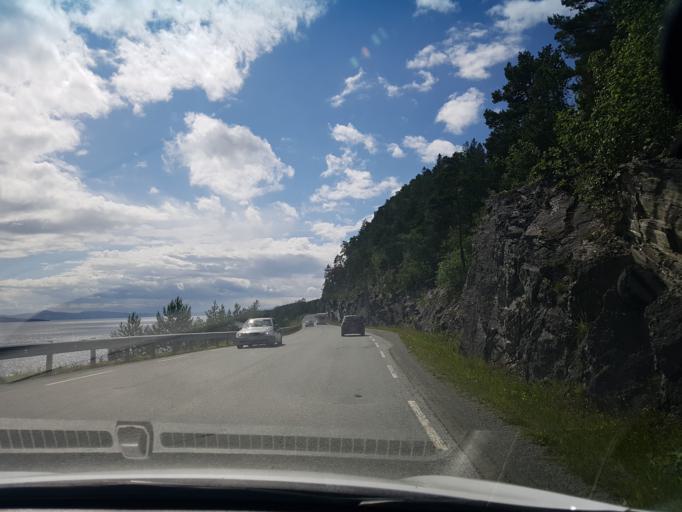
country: NO
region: Nord-Trondelag
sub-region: Frosta
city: Frosta
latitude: 63.6030
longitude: 10.8737
